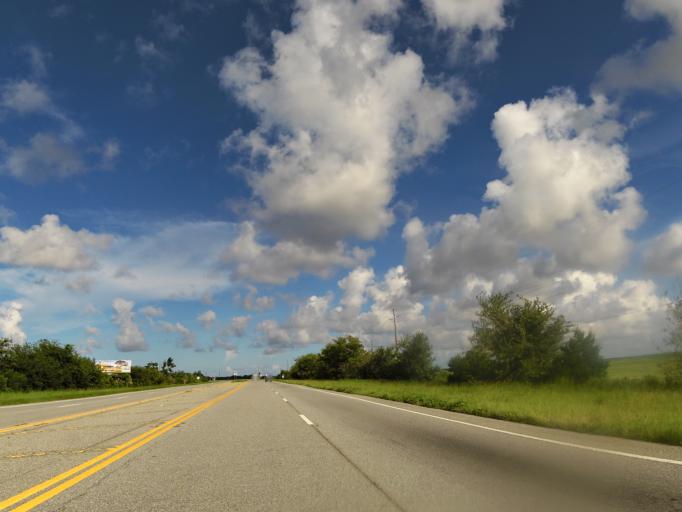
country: US
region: Georgia
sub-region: Glynn County
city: Brunswick
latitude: 31.1064
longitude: -81.5029
